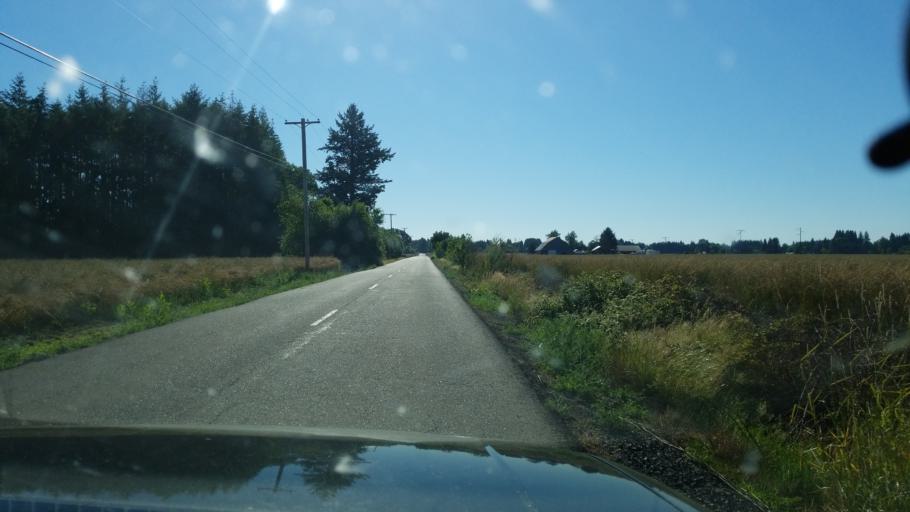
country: US
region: Oregon
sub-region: Yamhill County
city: McMinnville
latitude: 45.2449
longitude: -123.2113
